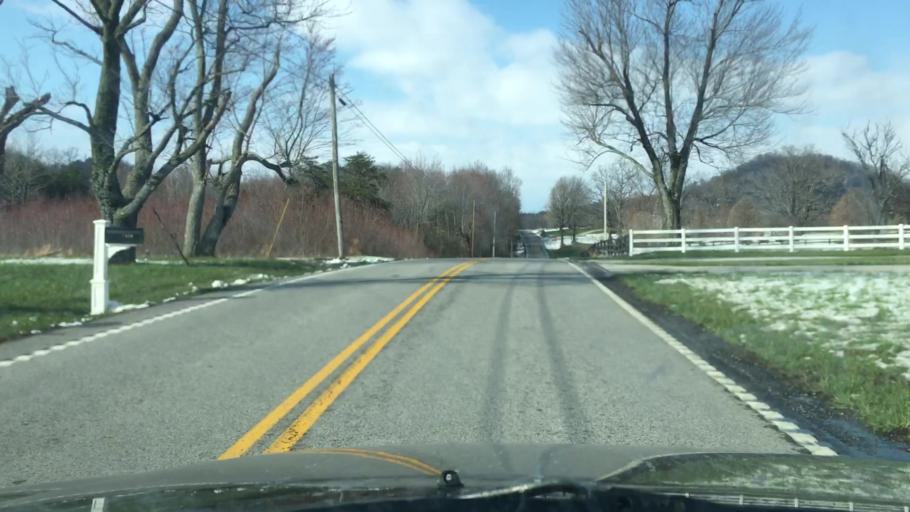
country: US
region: Kentucky
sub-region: Marion County
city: Lebanon
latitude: 37.5180
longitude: -85.3025
